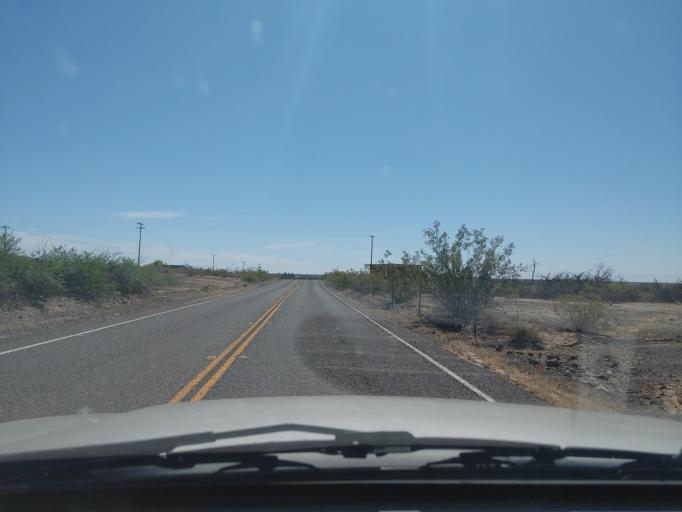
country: US
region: Arizona
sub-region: Maricopa County
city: Gila Bend
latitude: 32.9846
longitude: -113.3269
